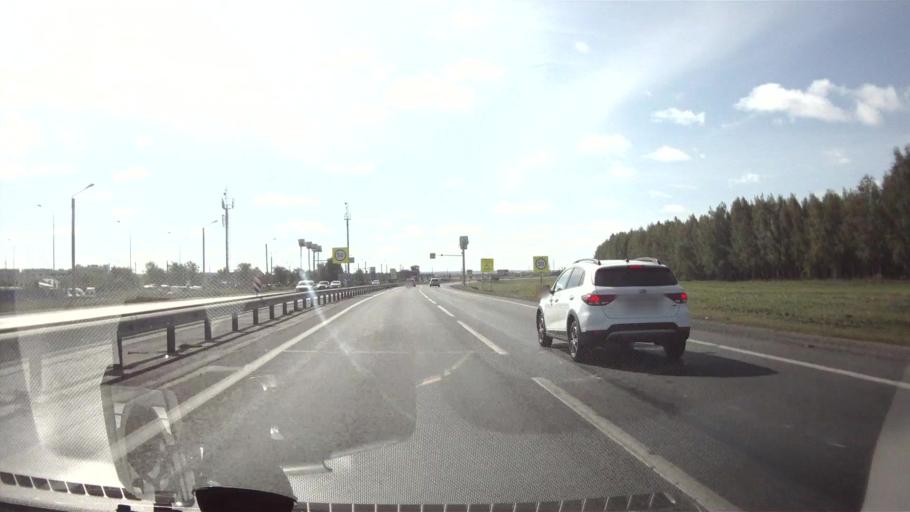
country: RU
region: Ulyanovsk
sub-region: Ulyanovskiy Rayon
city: Ulyanovsk
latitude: 54.2768
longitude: 48.2602
